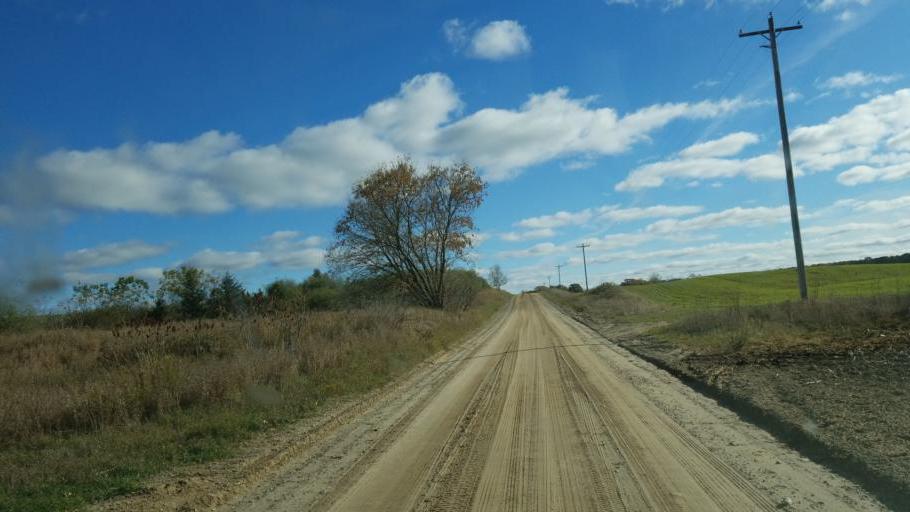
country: US
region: Michigan
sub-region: Montcalm County
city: Edmore
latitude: 43.4660
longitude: -85.0153
